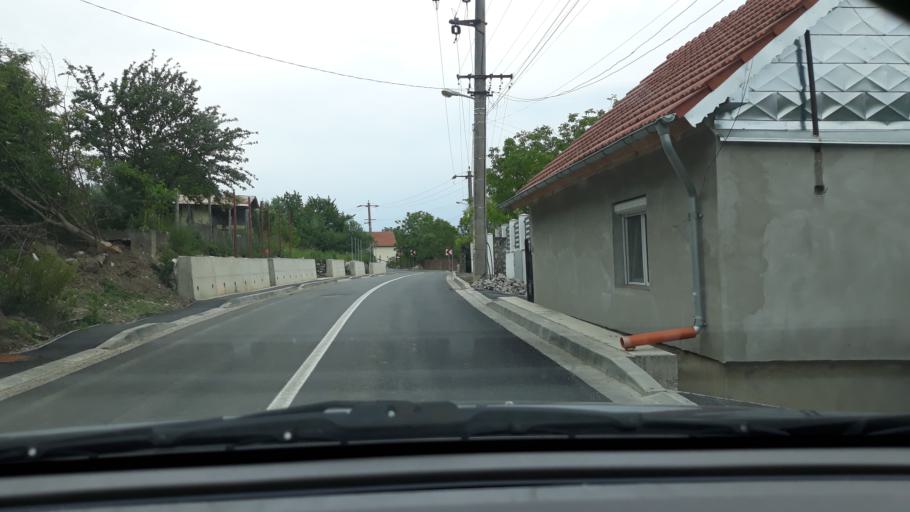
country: RO
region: Bihor
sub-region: Comuna Osorheiu
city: Osorheiu
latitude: 47.0588
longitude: 22.0098
